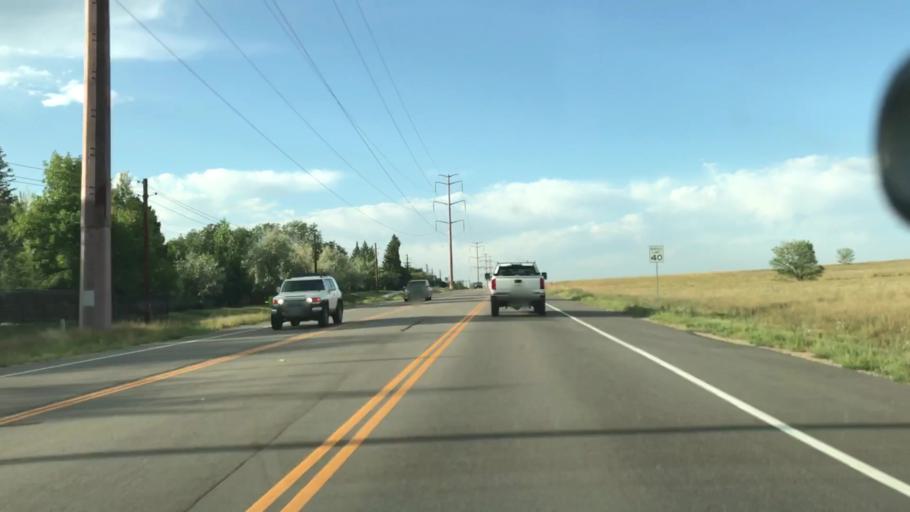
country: US
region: Colorado
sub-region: Boulder County
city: Gunbarrel
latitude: 40.0632
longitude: -105.1784
